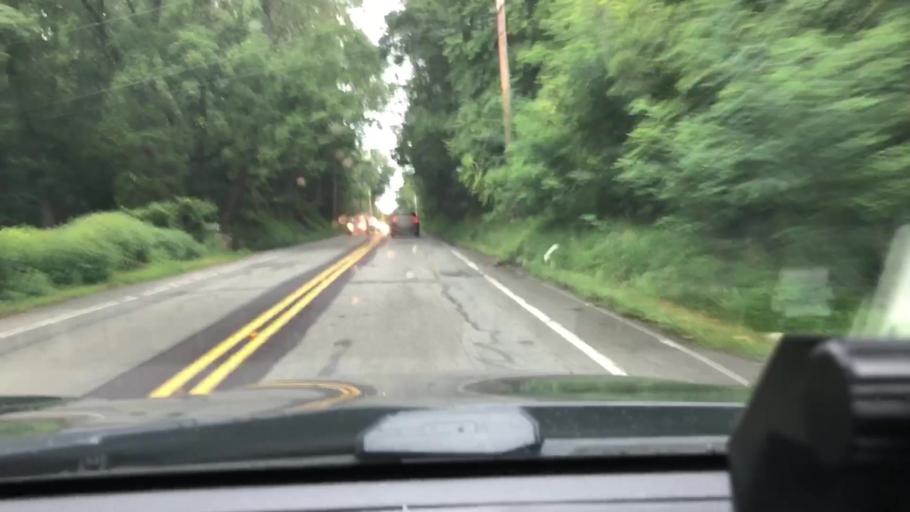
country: US
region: Pennsylvania
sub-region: Montgomery County
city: Red Hill
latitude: 40.3443
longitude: -75.5444
